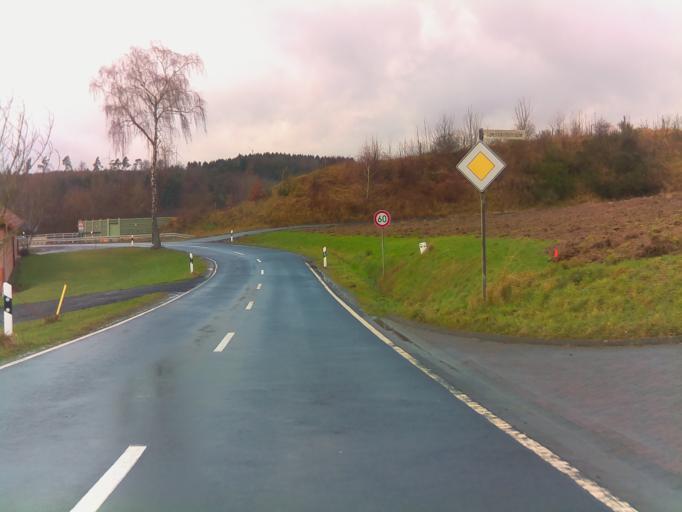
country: DE
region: Hesse
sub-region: Regierungsbezirk Kassel
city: Flieden
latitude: 50.4084
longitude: 9.5728
